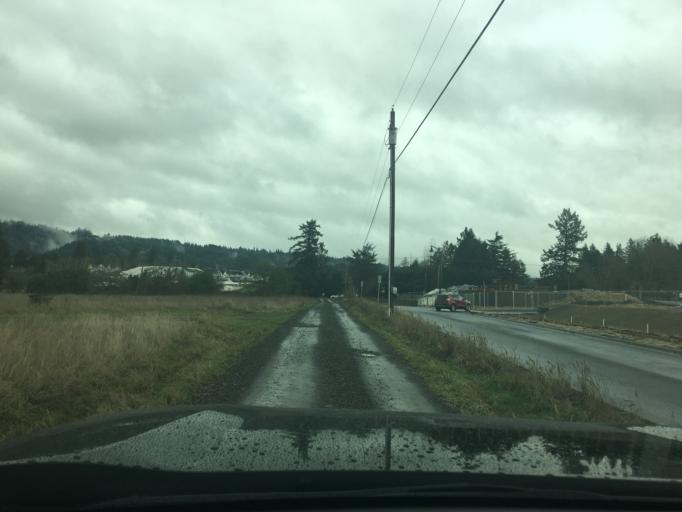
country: US
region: Oregon
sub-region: Washington County
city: Bethany
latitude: 45.5724
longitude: -122.8402
